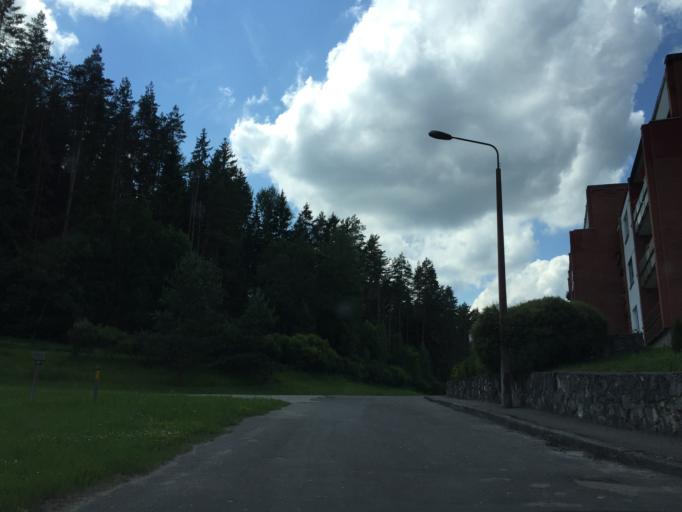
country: LV
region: Ligatne
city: Ligatne
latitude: 57.2560
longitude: 25.0770
